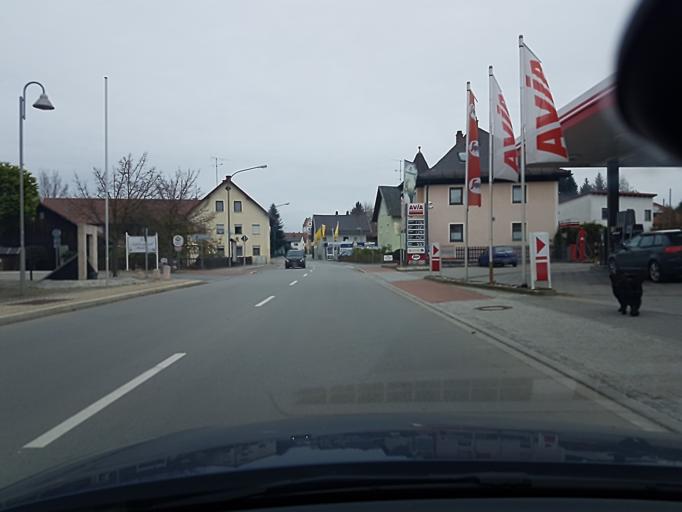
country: DE
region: Bavaria
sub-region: Lower Bavaria
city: Ergoldsbach
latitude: 48.7366
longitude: 12.1909
